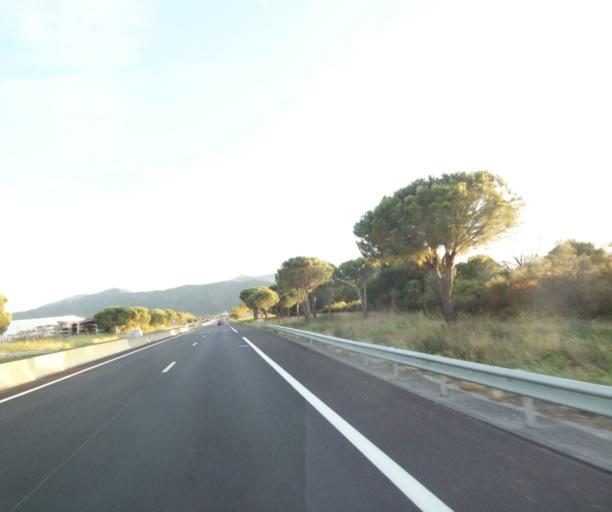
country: FR
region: Languedoc-Roussillon
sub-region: Departement des Pyrenees-Orientales
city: Argelers
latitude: 42.5586
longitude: 3.0061
